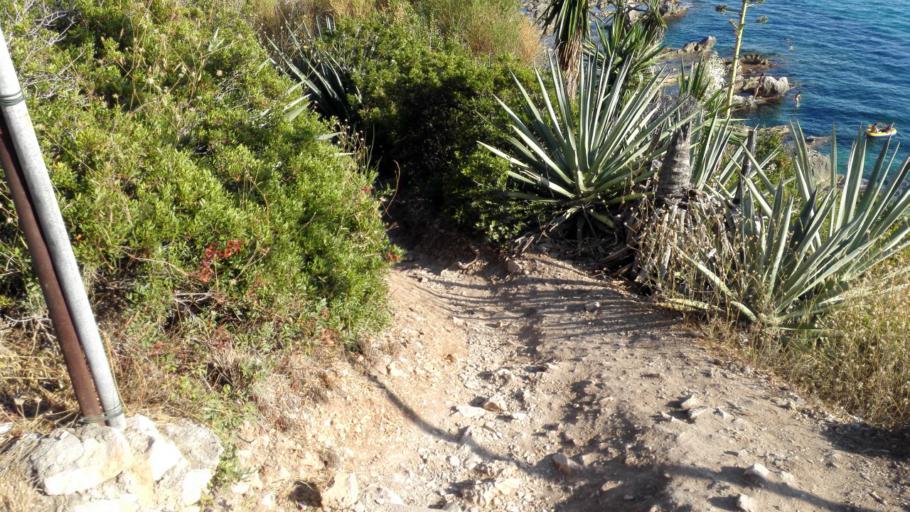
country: FR
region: Provence-Alpes-Cote d'Azur
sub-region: Departement des Alpes-Maritimes
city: Menton
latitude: 43.7838
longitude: 7.5383
